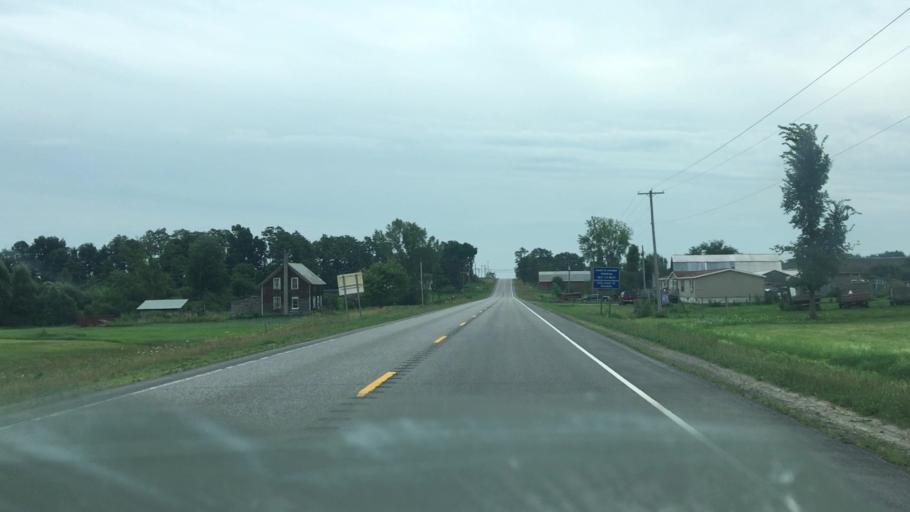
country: US
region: New York
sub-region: Clinton County
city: Morrisonville
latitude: 44.6481
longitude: -73.5685
